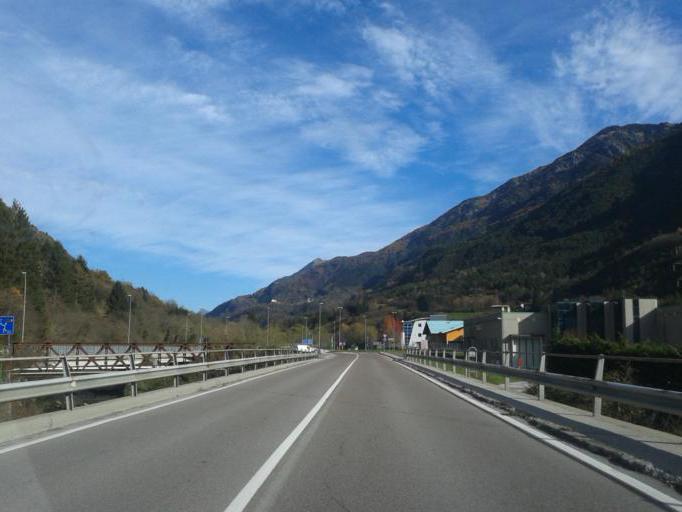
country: IT
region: Trentino-Alto Adige
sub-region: Provincia di Trento
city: Cimego
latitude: 45.9147
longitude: 10.6215
